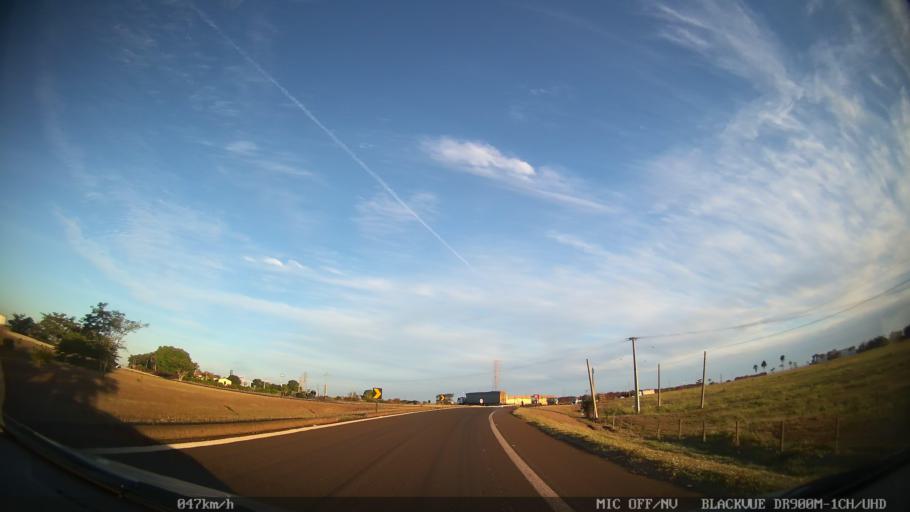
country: BR
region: Sao Paulo
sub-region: Catanduva
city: Catanduva
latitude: -21.1343
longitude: -49.0213
